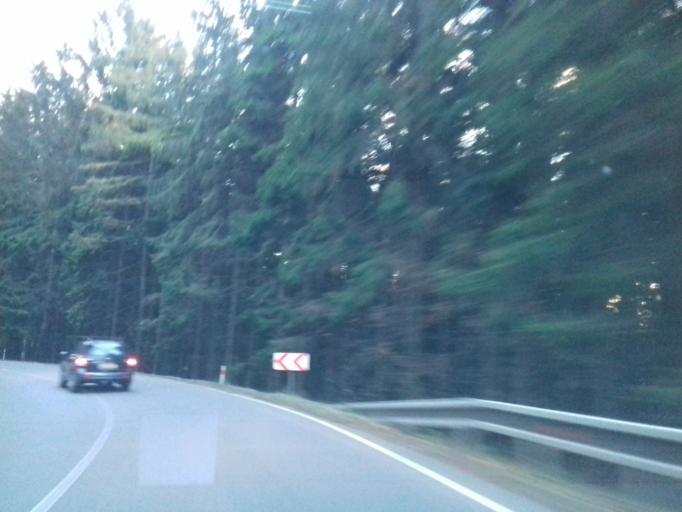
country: CZ
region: Pardubicky
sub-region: Okres Chrudim
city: Hlinsko
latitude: 49.7490
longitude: 15.8964
